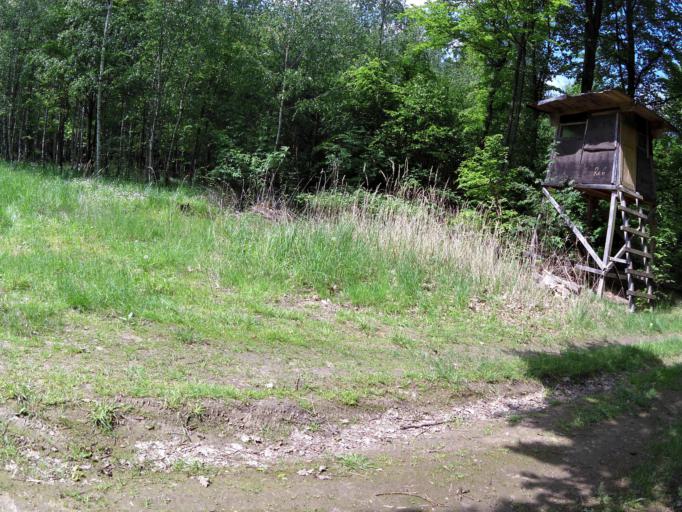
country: DE
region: Bavaria
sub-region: Regierungsbezirk Unterfranken
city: Kist
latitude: 49.7367
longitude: 9.8593
